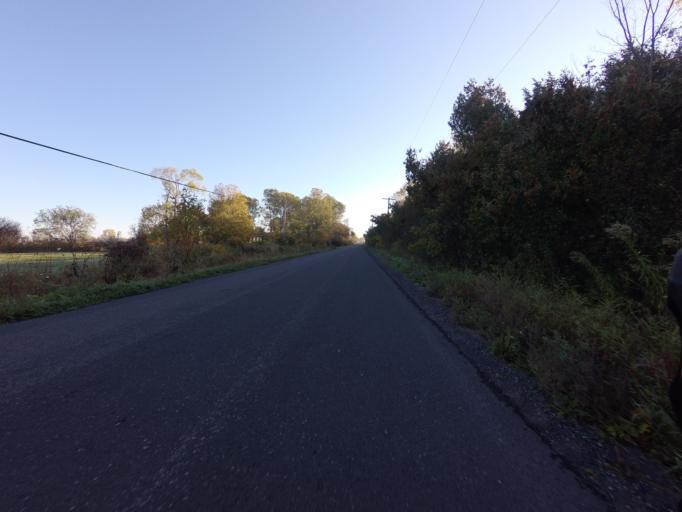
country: CA
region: Ontario
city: Quinte West
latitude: 44.0096
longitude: -77.5112
